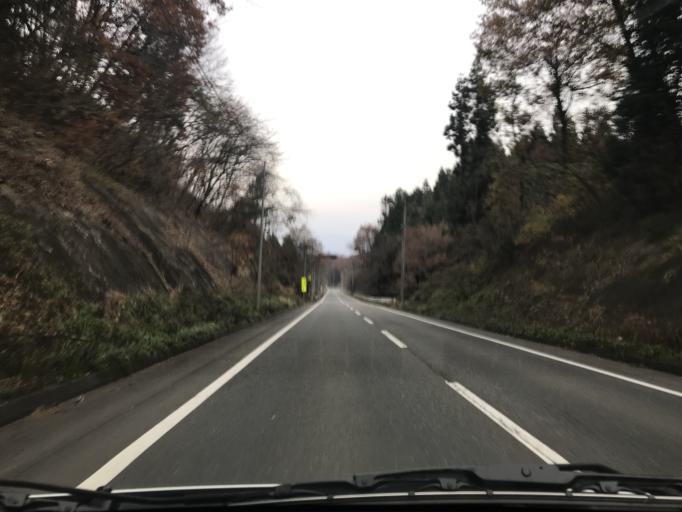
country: JP
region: Iwate
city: Kitakami
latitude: 39.2859
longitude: 141.2267
